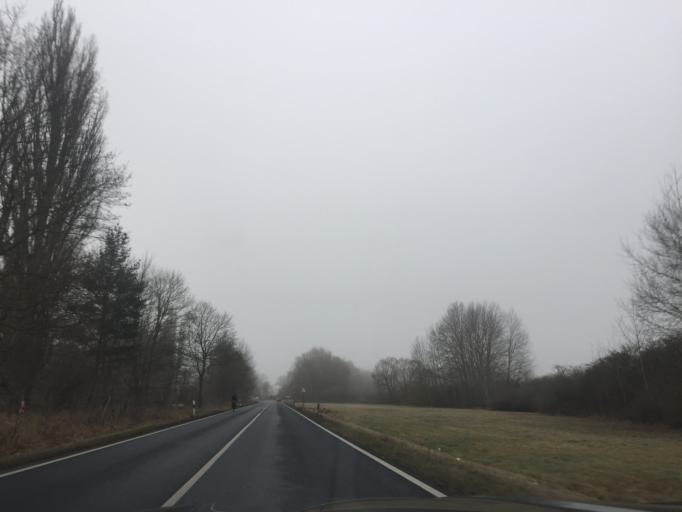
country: DE
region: Brandenburg
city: Hennigsdorf
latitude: 52.6290
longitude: 13.1433
